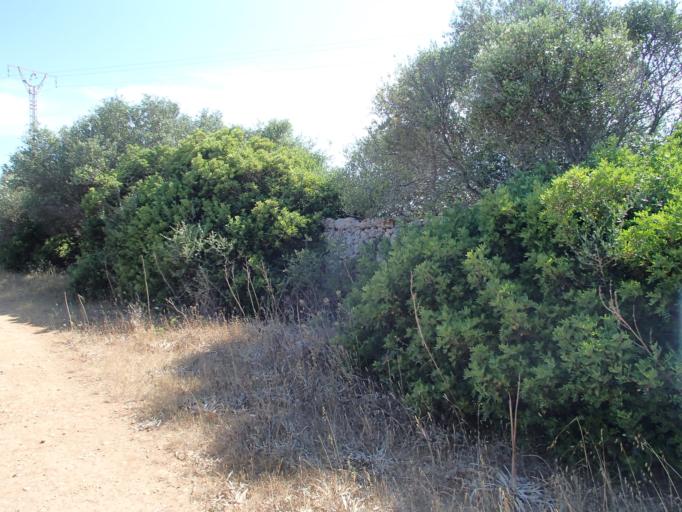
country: ES
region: Balearic Islands
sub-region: Illes Balears
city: Es Castell
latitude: 39.8457
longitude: 4.2934
